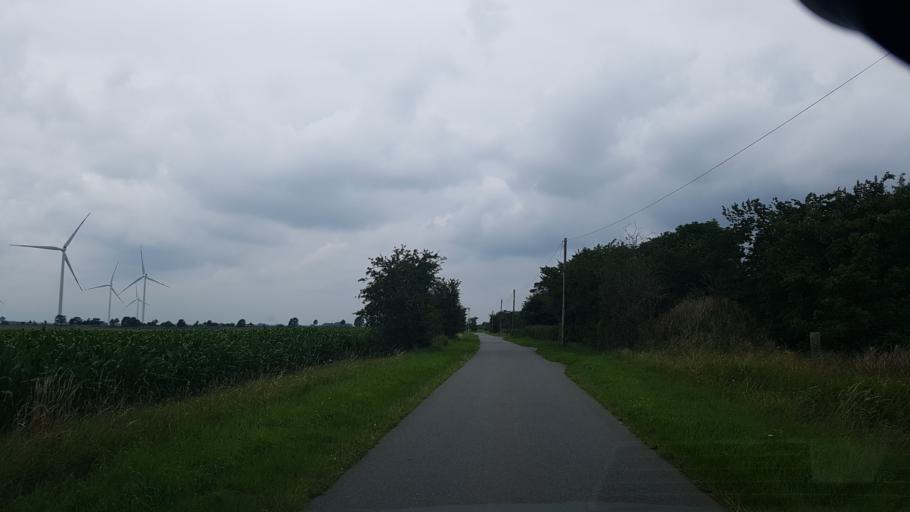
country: DE
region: Schleswig-Holstein
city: Ellhoft
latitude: 54.8970
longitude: 8.9230
